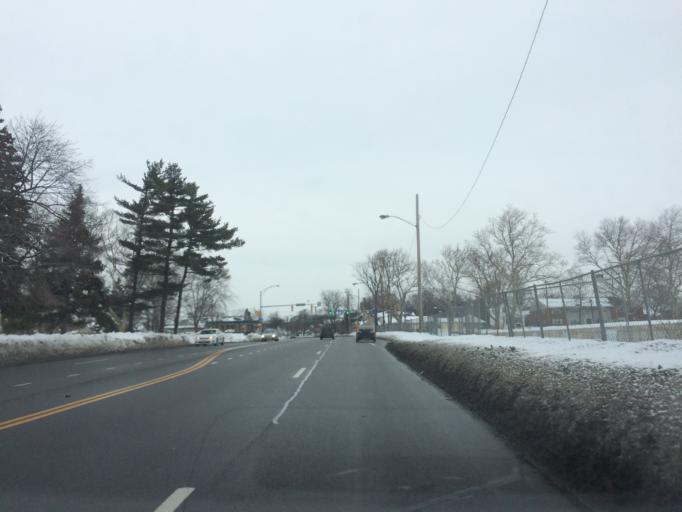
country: US
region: New York
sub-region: Monroe County
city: Rochester
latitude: 43.1134
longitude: -77.6160
